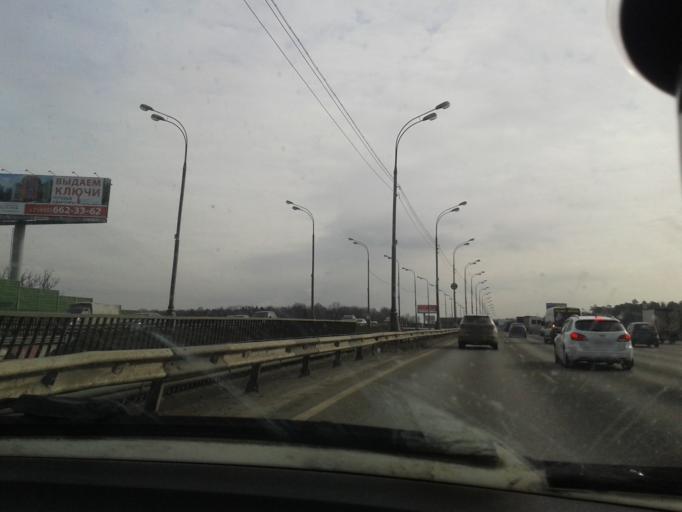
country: RU
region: Moscow
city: Khimki
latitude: 55.8826
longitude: 37.4538
